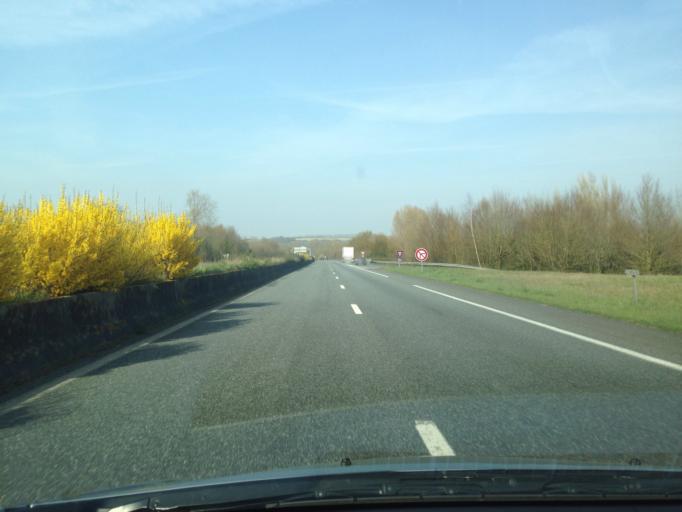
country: FR
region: Picardie
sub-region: Departement de la Somme
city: Abbeville
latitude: 50.1064
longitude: 1.7868
